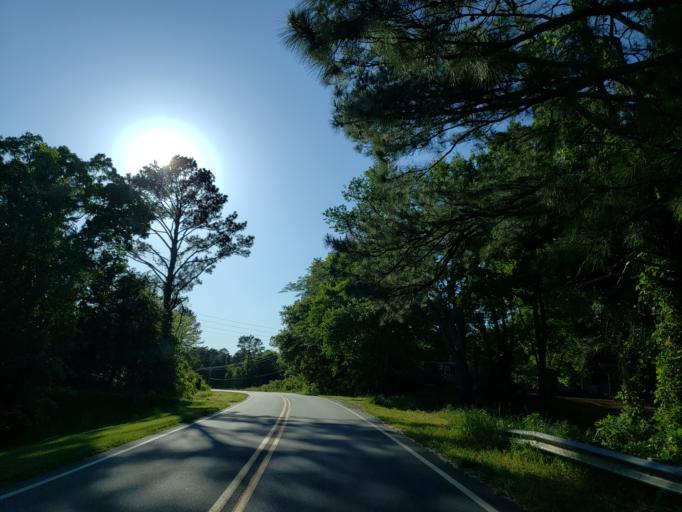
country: US
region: Georgia
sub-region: Haralson County
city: Buchanan
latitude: 33.8099
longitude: -85.2202
